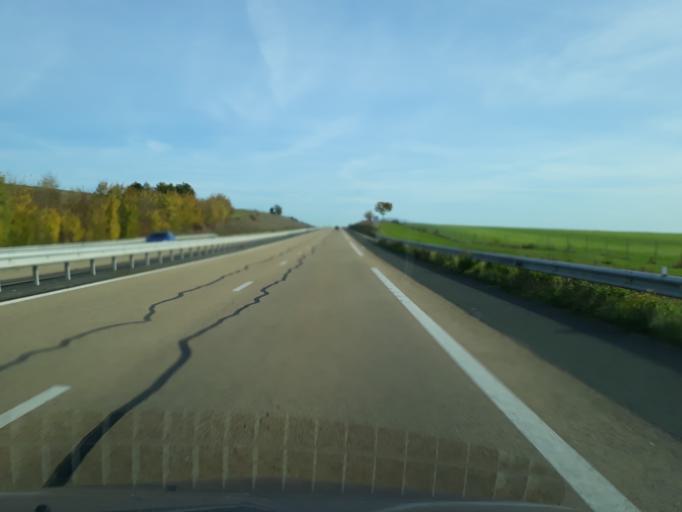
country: FR
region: Champagne-Ardenne
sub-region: Departement de l'Aube
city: Aix-en-Othe
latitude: 48.2680
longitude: 3.7522
